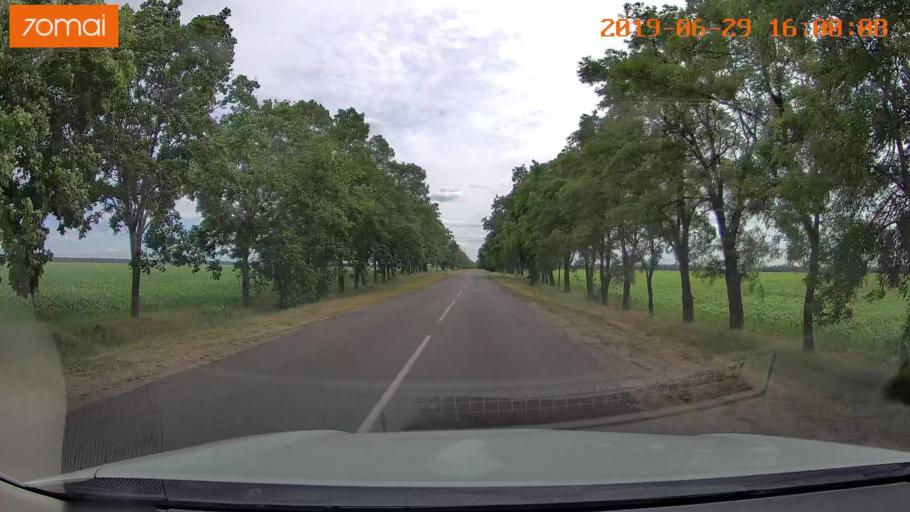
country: BY
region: Brest
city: Luninyets
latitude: 52.2636
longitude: 27.0176
